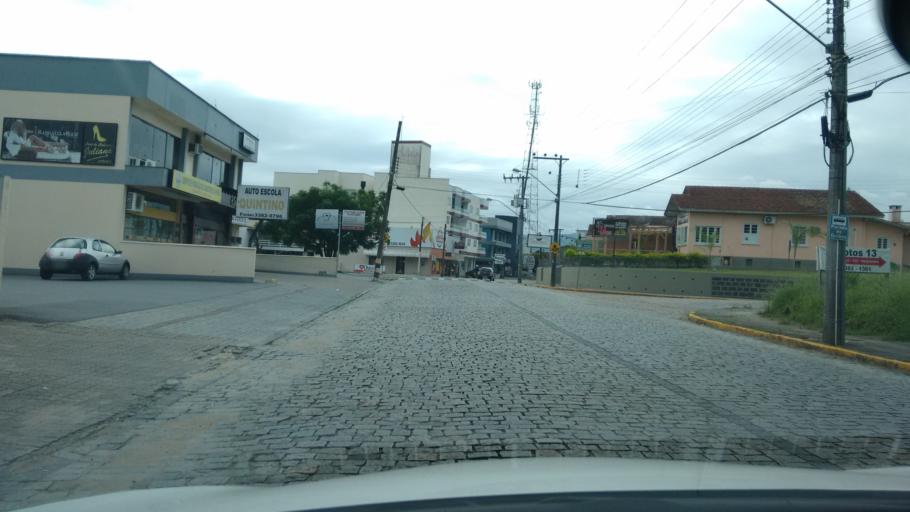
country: BR
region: Santa Catarina
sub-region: Timbo
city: Timbo
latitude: -26.8273
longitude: -49.2703
